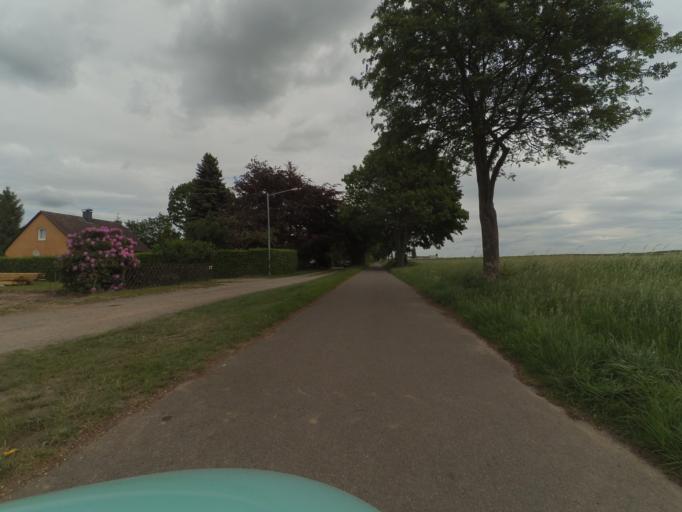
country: DE
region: Lower Saxony
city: Hagenburg
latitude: 52.4540
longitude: 9.3725
